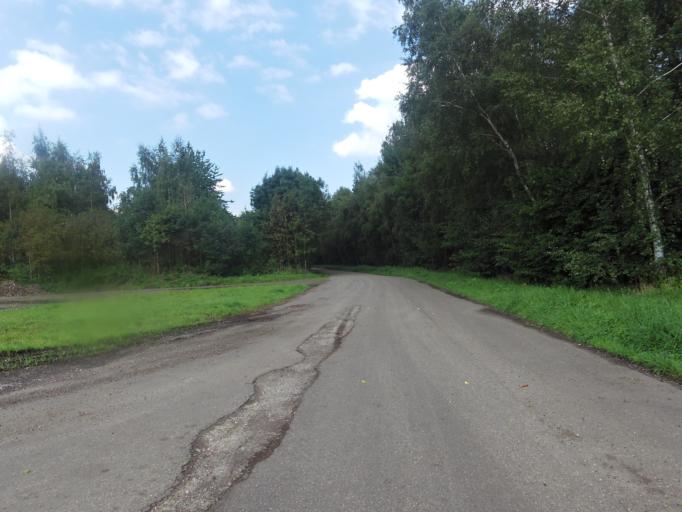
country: NL
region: Limburg
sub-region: Gemeente Nuth
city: Nuth
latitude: 50.9195
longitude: 5.8950
